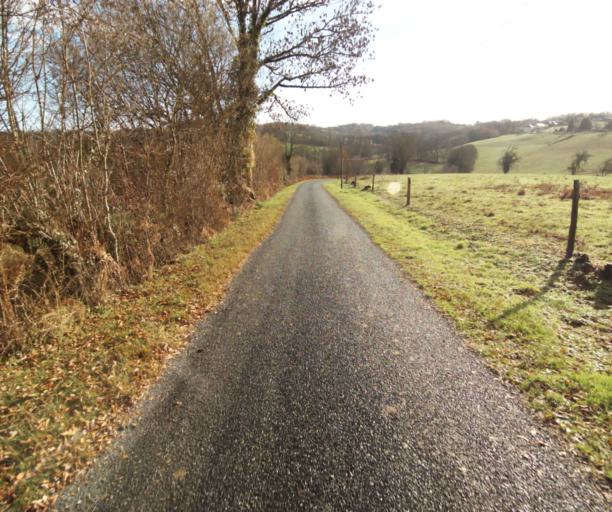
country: FR
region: Limousin
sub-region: Departement de la Correze
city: Sainte-Fereole
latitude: 45.2530
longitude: 1.6041
